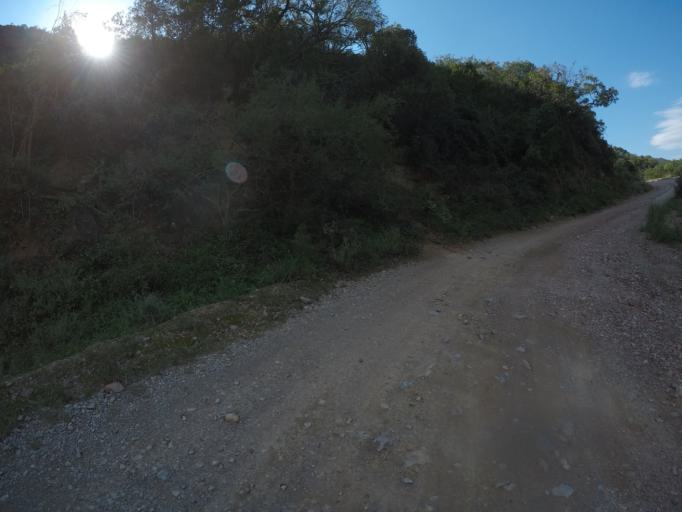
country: ZA
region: Eastern Cape
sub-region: Cacadu District Municipality
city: Kareedouw
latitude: -33.6509
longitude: 24.3462
